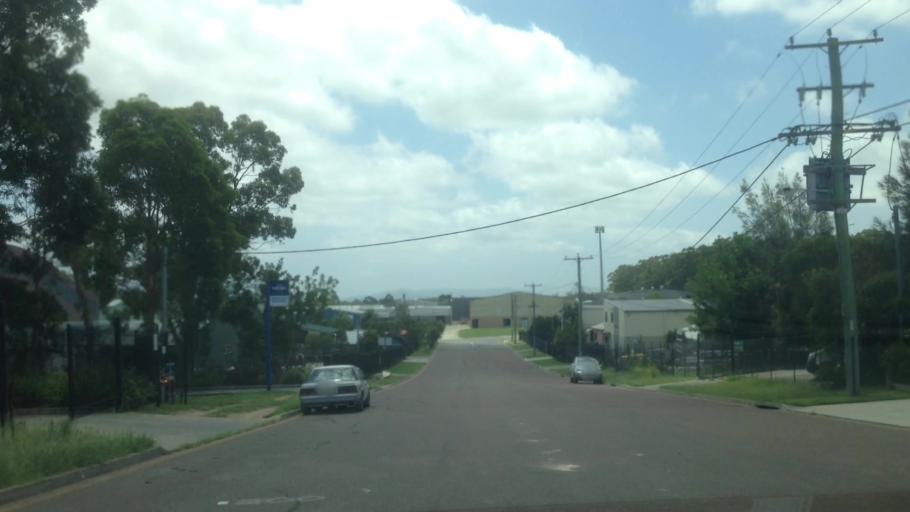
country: AU
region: New South Wales
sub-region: Lake Macquarie Shire
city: Dora Creek
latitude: -33.1198
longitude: 151.4732
